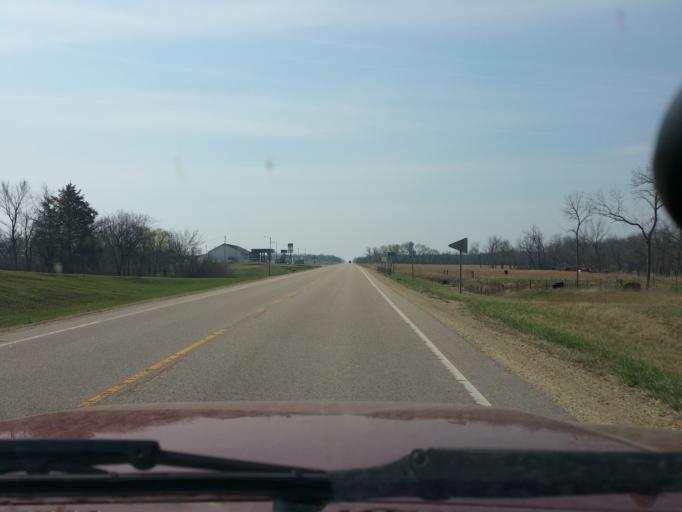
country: US
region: Kansas
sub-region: Marshall County
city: Blue Rapids
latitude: 39.4336
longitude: -96.7644
